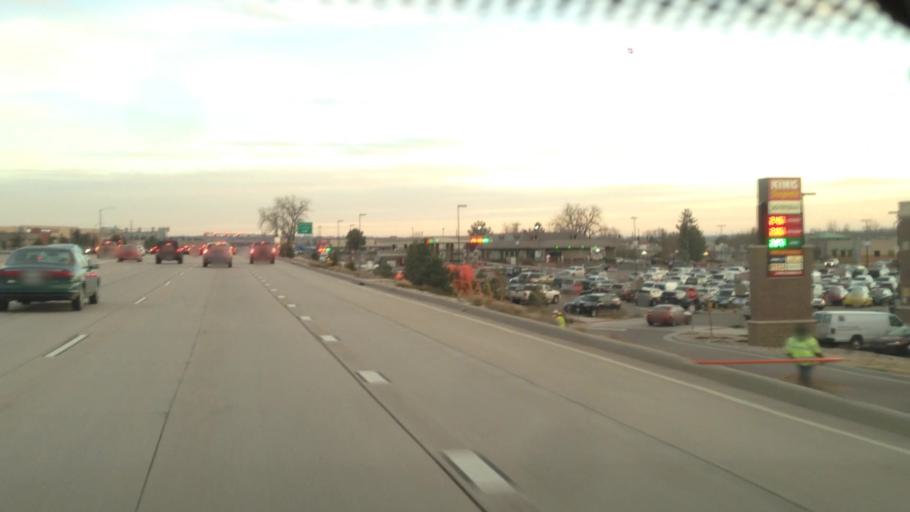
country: US
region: Colorado
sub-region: Douglas County
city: Stonegate
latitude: 39.5608
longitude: -104.7817
